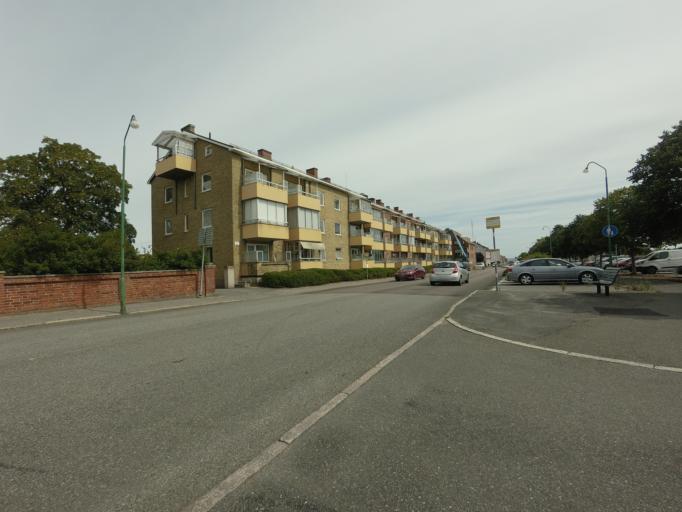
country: SE
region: Skane
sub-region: Simrishamns Kommun
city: Simrishamn
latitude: 55.5534
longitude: 14.3489
